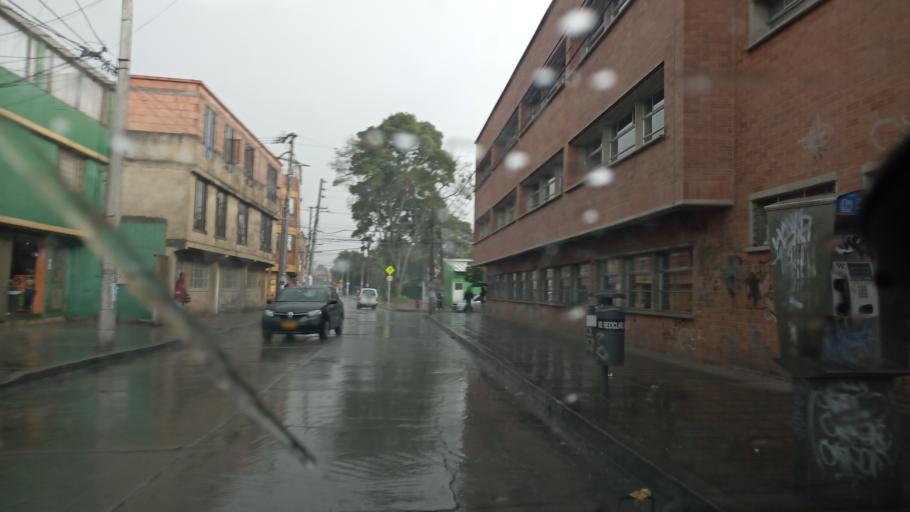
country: CO
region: Cundinamarca
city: Funza
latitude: 4.6728
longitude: -74.1392
